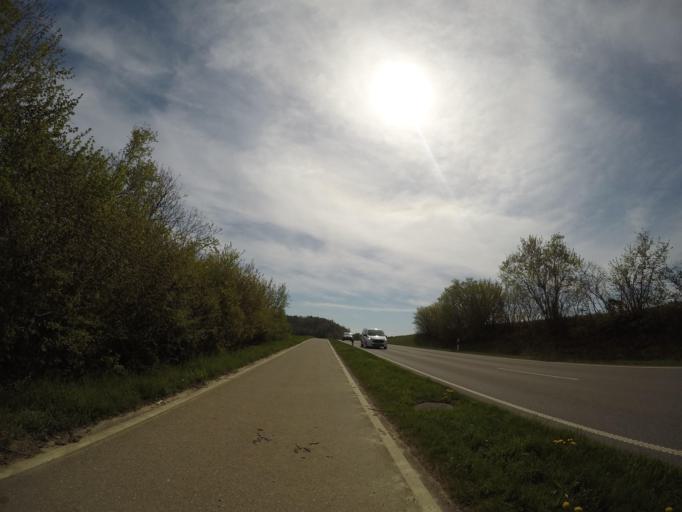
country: DE
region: Baden-Wuerttemberg
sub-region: Tuebingen Region
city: Boms
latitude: 47.9571
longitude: 9.5125
